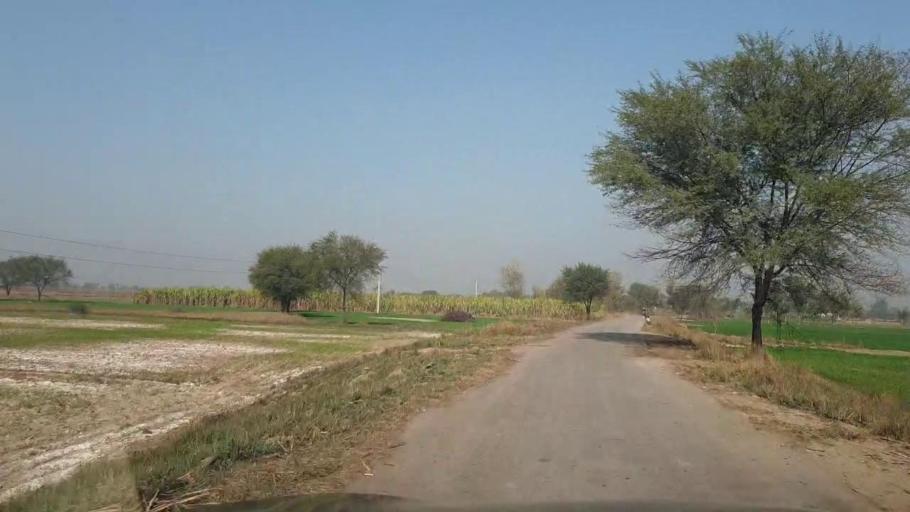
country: PK
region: Sindh
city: Ubauro
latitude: 28.1330
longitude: 69.7694
